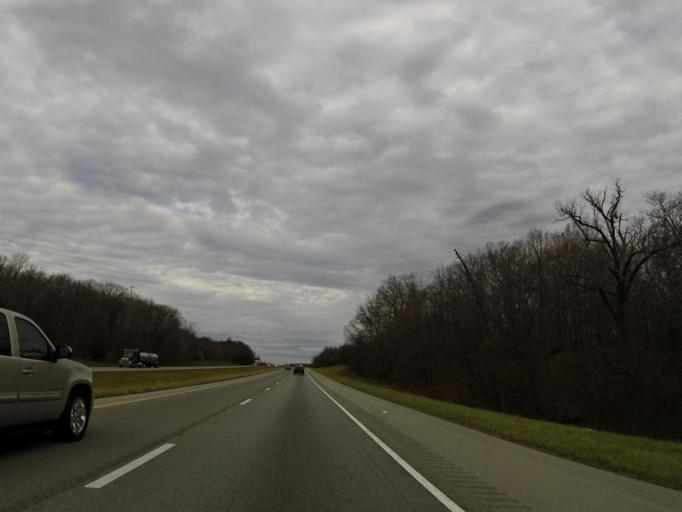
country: US
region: Illinois
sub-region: Clinton County
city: Wamac
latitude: 38.3701
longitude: -89.0939
